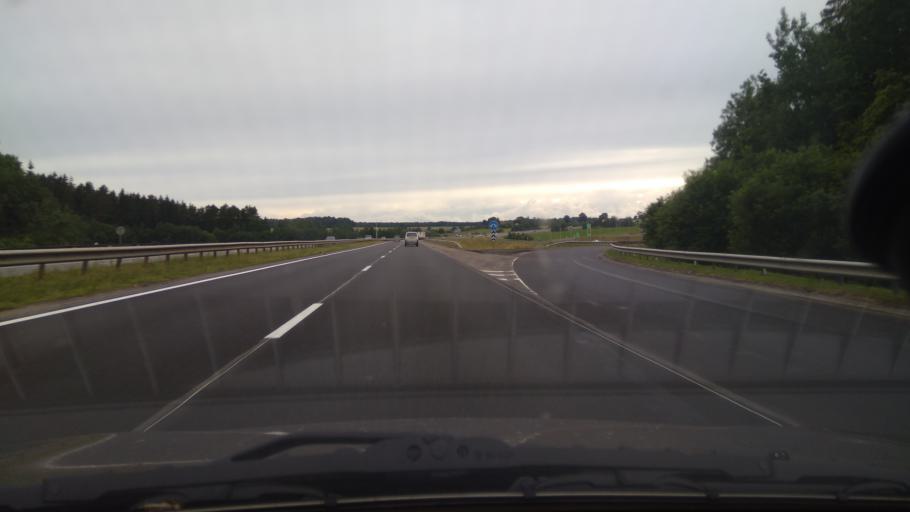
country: BY
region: Minsk
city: Khatsyezhyna
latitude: 53.9136
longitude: 27.2614
